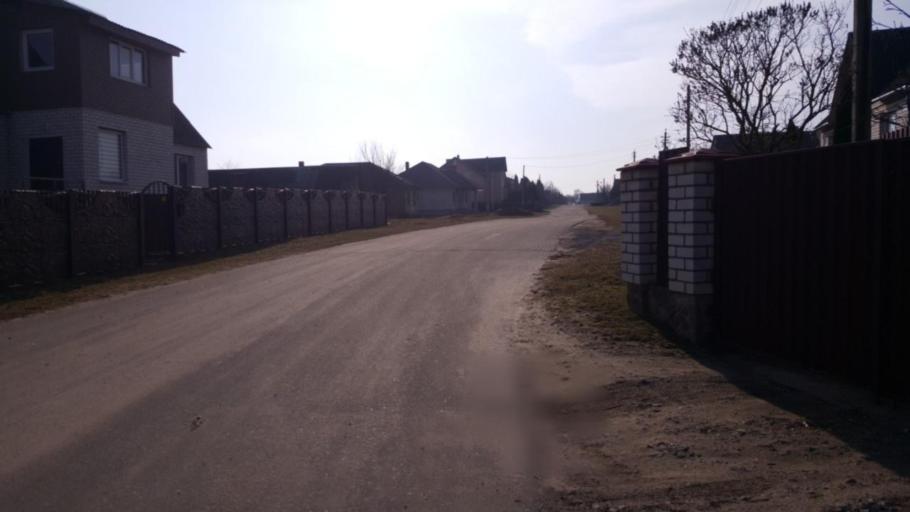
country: BY
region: Brest
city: Kamyanyets
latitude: 52.4010
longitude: 23.8396
